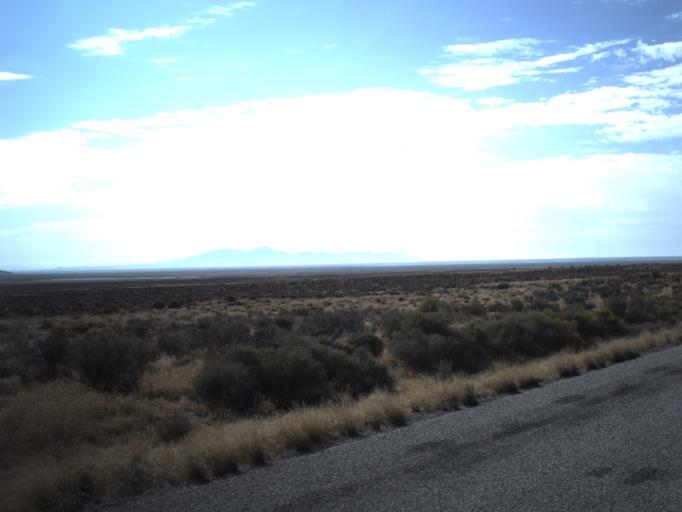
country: US
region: Utah
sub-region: Tooele County
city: Wendover
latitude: 41.5232
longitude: -113.5965
